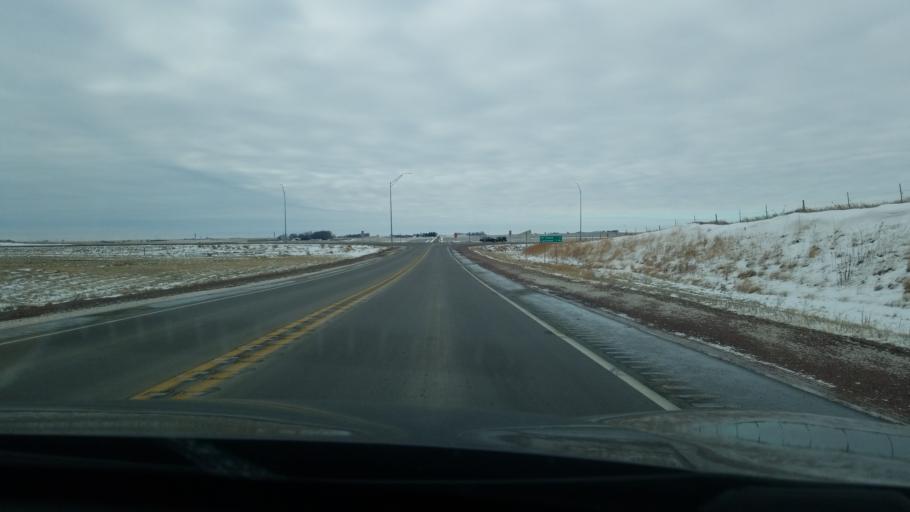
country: US
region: South Dakota
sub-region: Lincoln County
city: Canton
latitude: 43.4331
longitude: -96.4266
